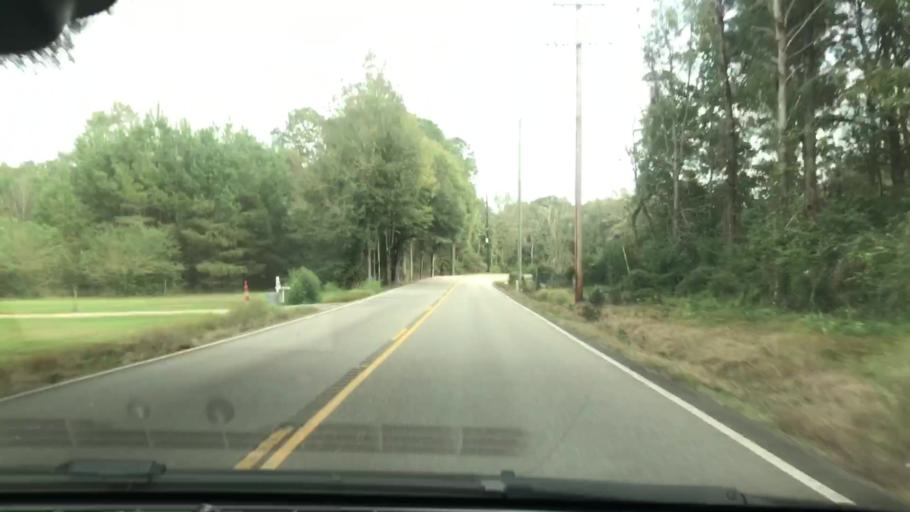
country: US
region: Louisiana
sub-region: Saint Tammany Parish
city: Abita Springs
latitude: 30.5343
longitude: -89.8868
